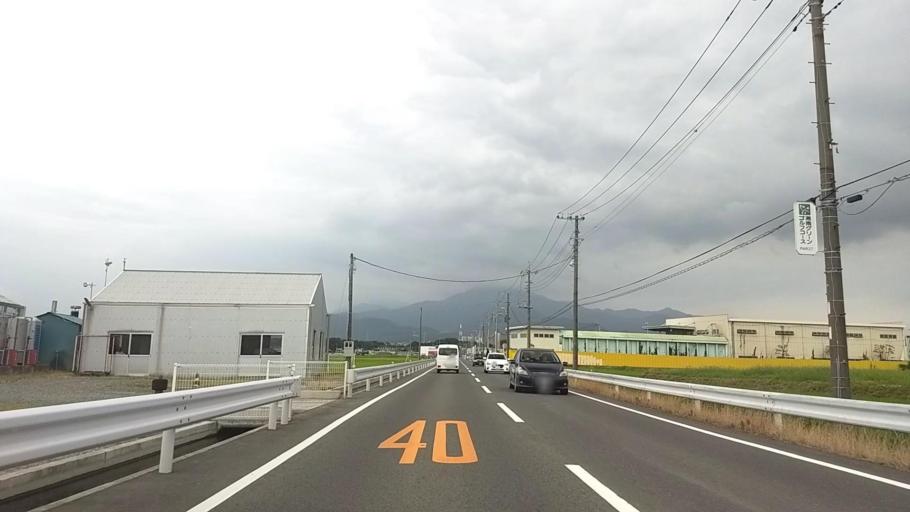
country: JP
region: Kanagawa
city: Isehara
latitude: 35.3833
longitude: 139.3380
